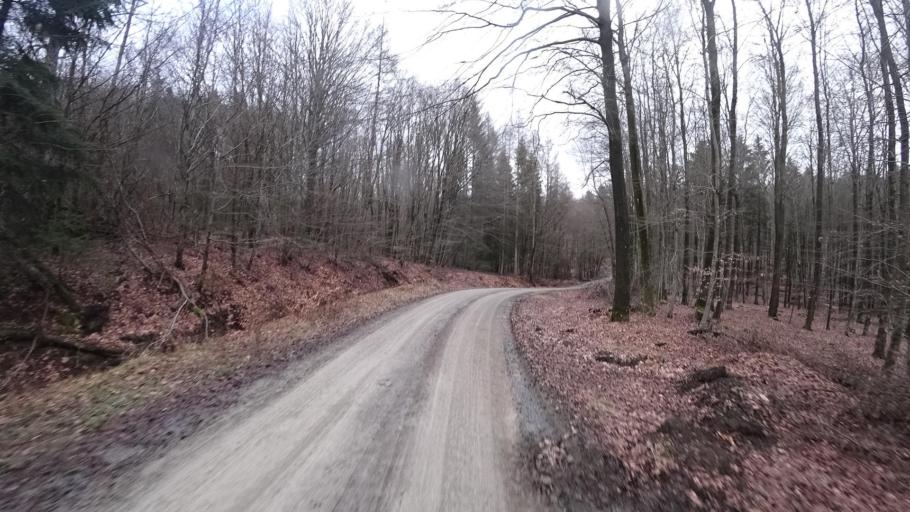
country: DE
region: Rheinland-Pfalz
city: Dernbach
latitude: 50.4222
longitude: 7.7628
